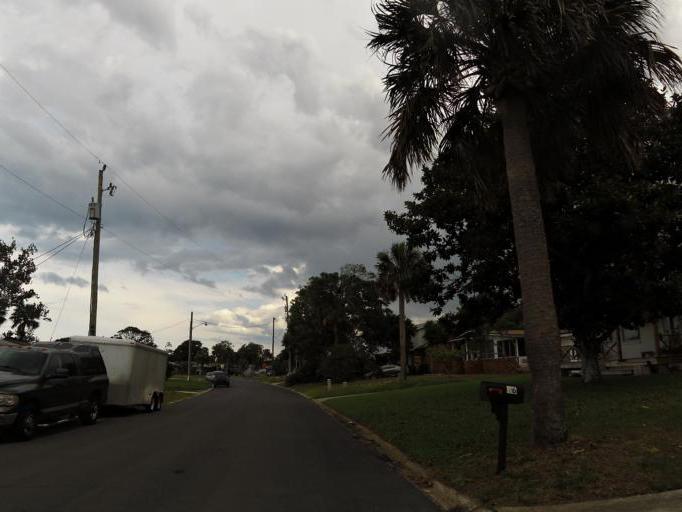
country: US
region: Florida
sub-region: Duval County
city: Jacksonville Beach
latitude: 30.2703
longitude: -81.3925
